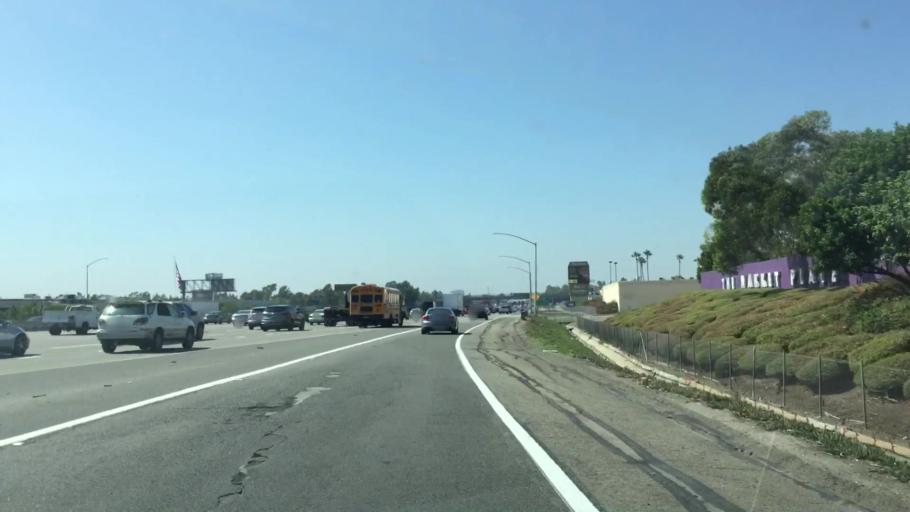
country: US
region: California
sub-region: Orange County
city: Tustin
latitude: 33.7212
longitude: -117.7967
